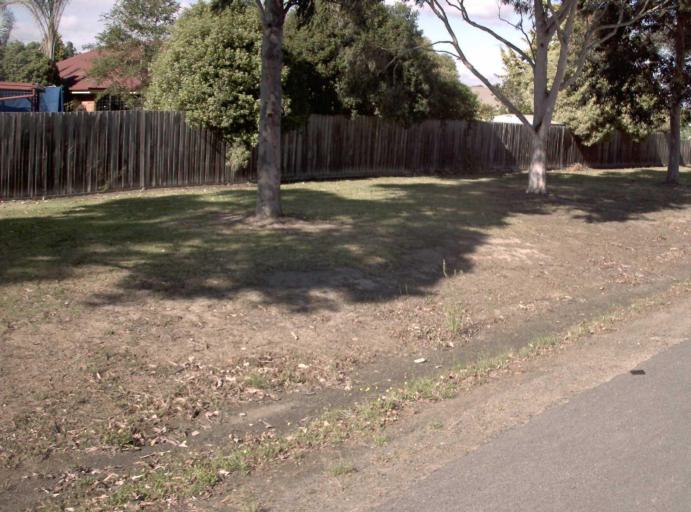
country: AU
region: Victoria
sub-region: Latrobe
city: Traralgon
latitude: -38.1910
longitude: 146.5115
